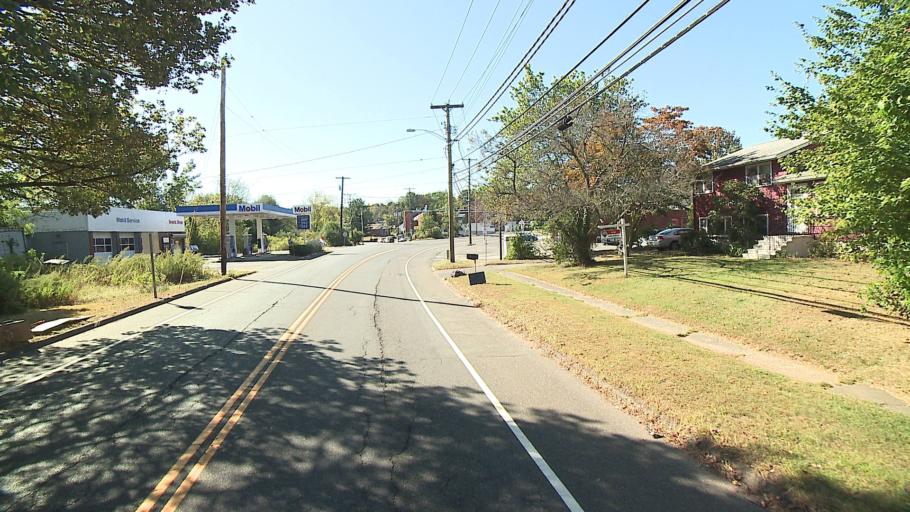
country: US
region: Connecticut
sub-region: New Haven County
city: West Haven
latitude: 41.2613
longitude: -72.9636
